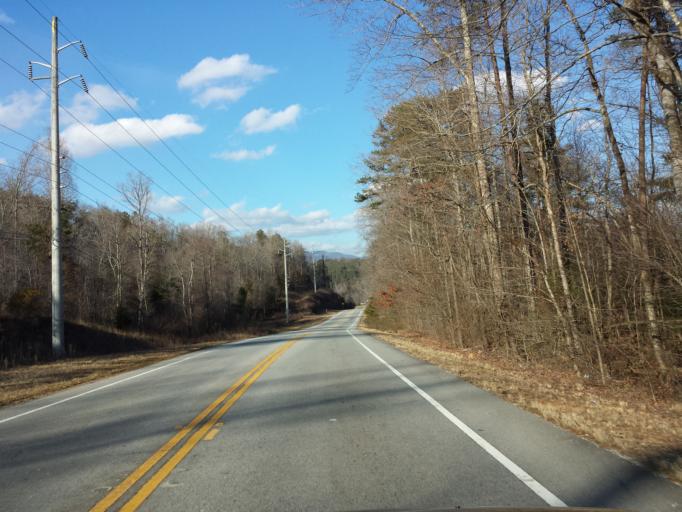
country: US
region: Georgia
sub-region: White County
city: Cleveland
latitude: 34.6787
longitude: -83.7133
